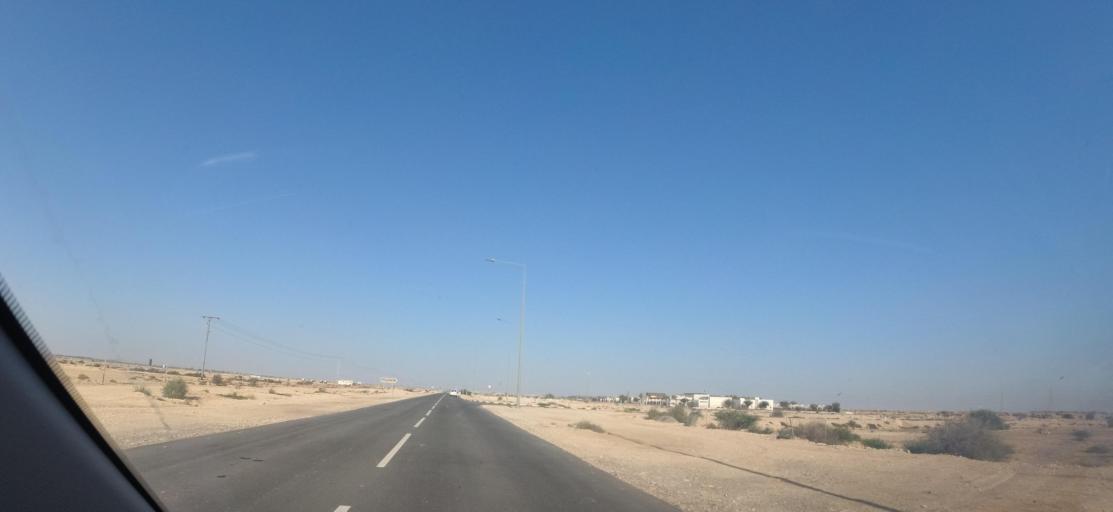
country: QA
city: Al Ghuwayriyah
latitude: 25.8431
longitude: 51.2635
